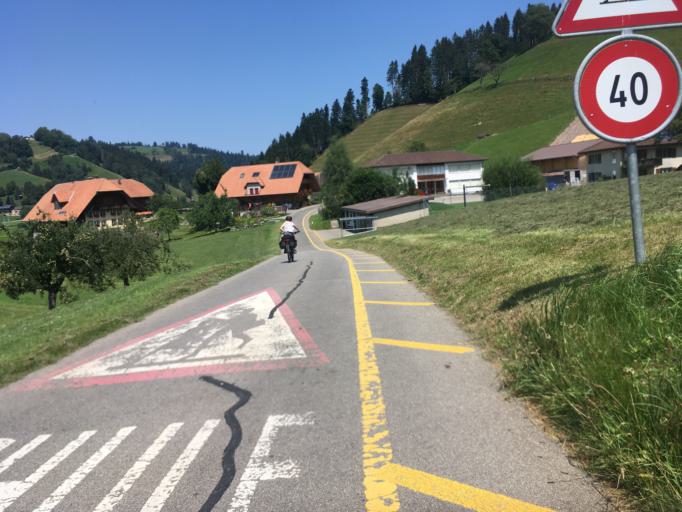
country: CH
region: Bern
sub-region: Bern-Mittelland District
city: Bowil
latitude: 46.8984
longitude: 7.7107
